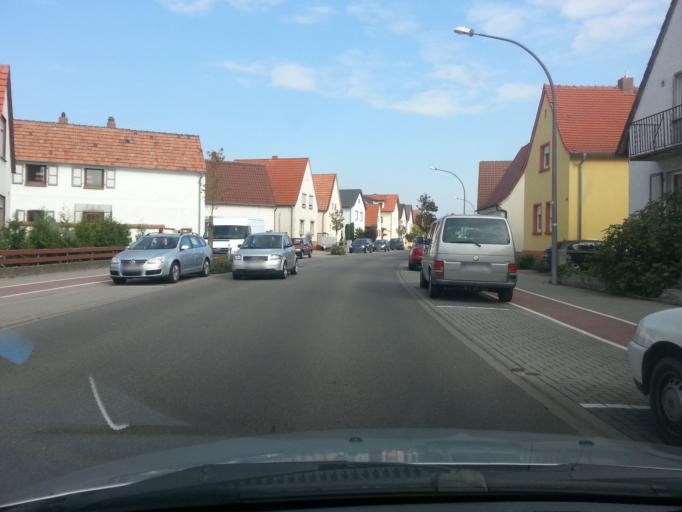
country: DE
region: Rheinland-Pfalz
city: Hassloch
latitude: 49.3539
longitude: 8.2485
